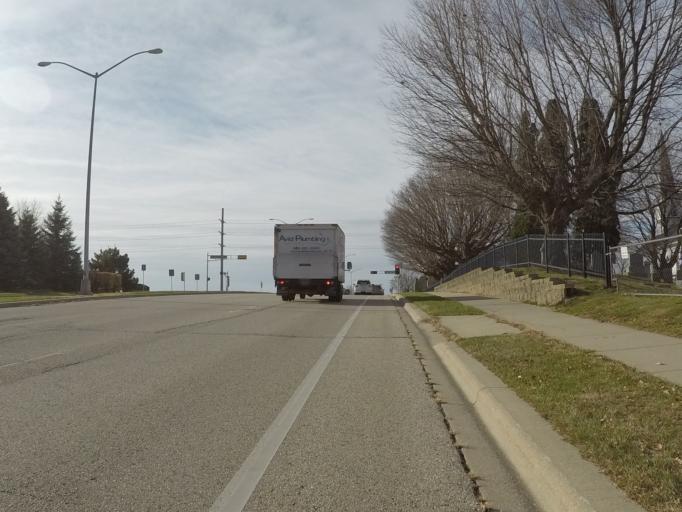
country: US
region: Wisconsin
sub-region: Dane County
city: Middleton
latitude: 43.0749
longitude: -89.5359
